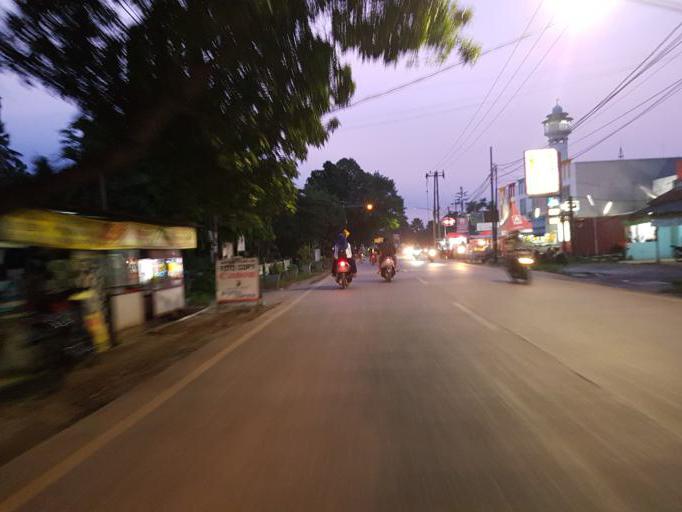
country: ID
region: West Java
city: Serpong
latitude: -6.3243
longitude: 106.6648
